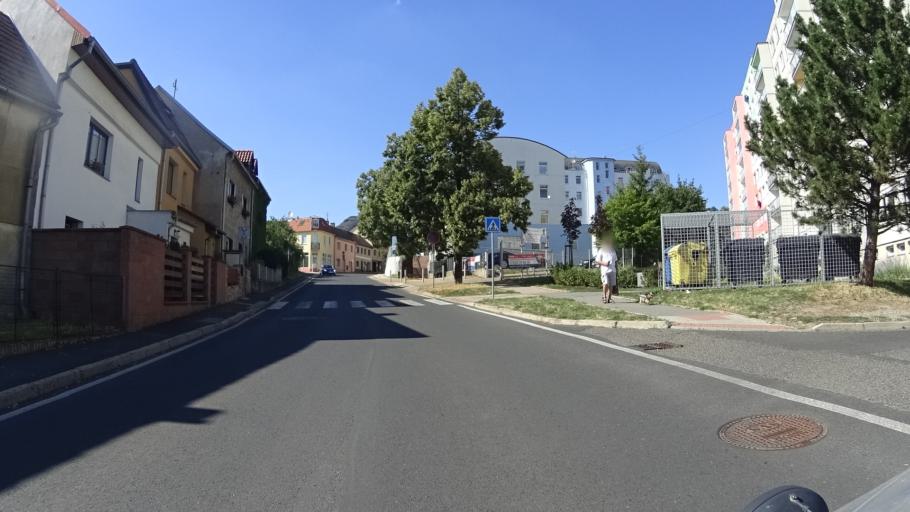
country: CZ
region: Ustecky
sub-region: Okres Litomerice
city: Litomerice
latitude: 50.5486
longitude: 14.1261
